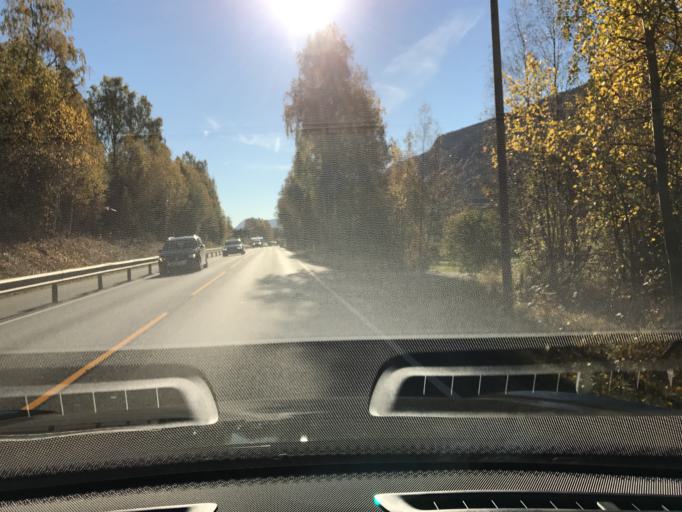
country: NO
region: Buskerud
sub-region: Gol
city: Gol
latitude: 60.6846
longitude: 9.0259
